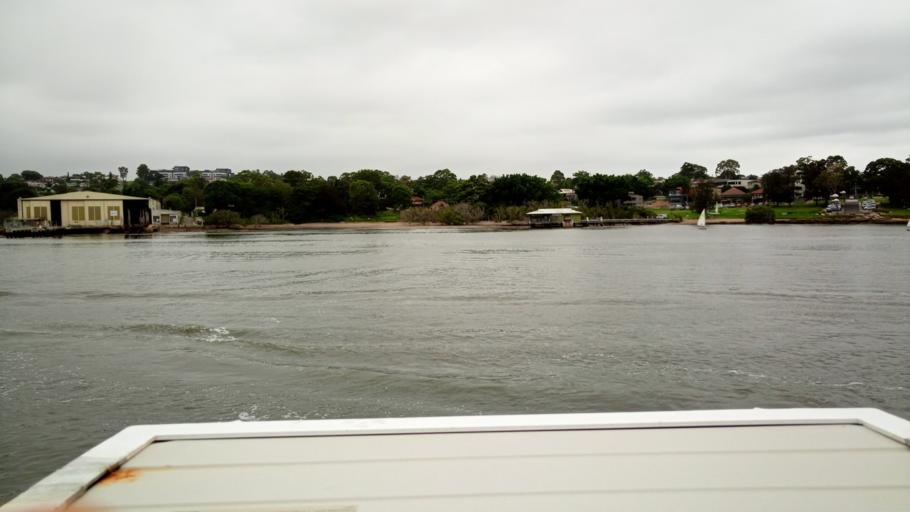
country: AU
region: New South Wales
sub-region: Canada Bay
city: Rhodes
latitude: -33.8288
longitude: 151.0979
